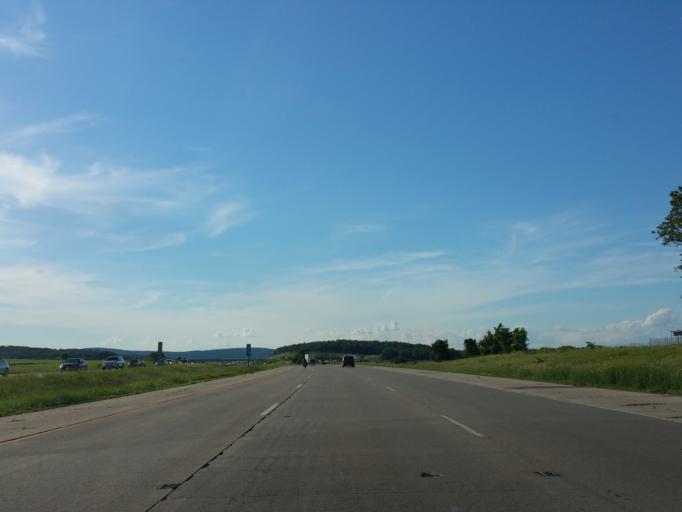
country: US
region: Wisconsin
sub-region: Columbia County
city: Poynette
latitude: 43.4134
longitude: -89.4687
